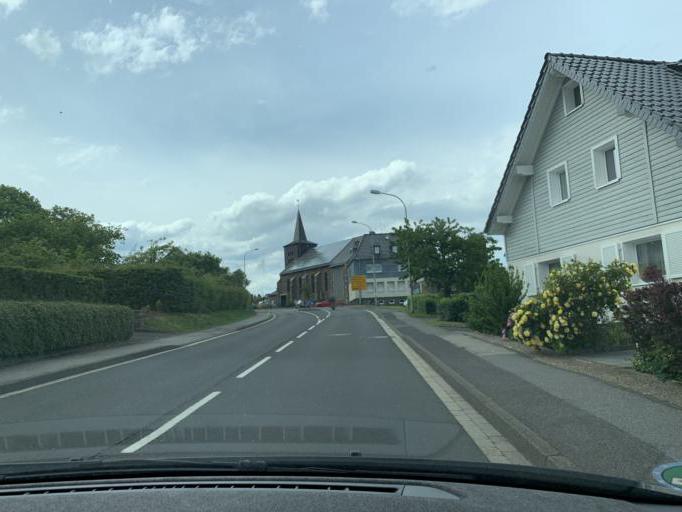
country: DE
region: North Rhine-Westphalia
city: Heimbach
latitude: 50.6584
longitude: 6.4109
